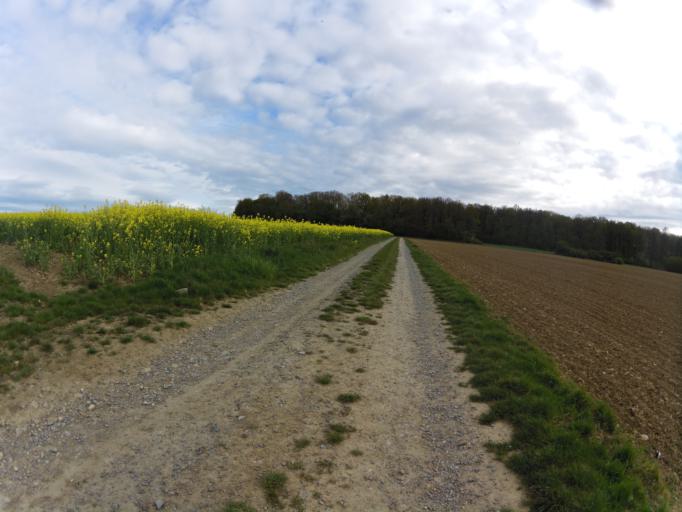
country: DE
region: Bavaria
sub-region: Regierungsbezirk Unterfranken
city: Prosselsheim
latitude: 49.8633
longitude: 10.1515
